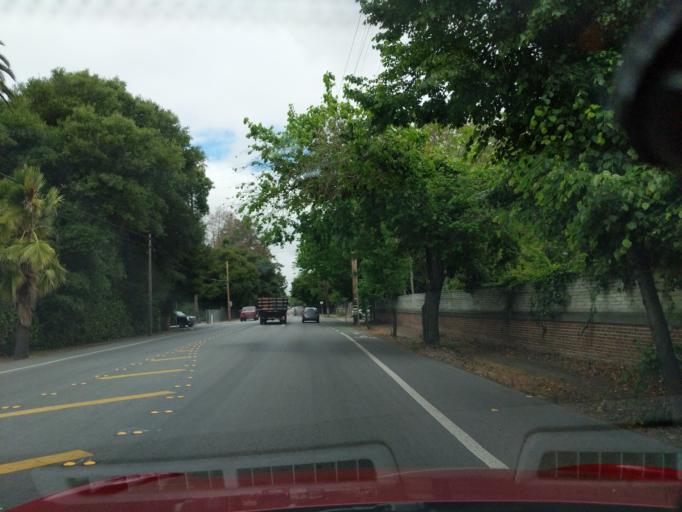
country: US
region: California
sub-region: San Mateo County
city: Menlo Park
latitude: 37.4632
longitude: -122.1810
